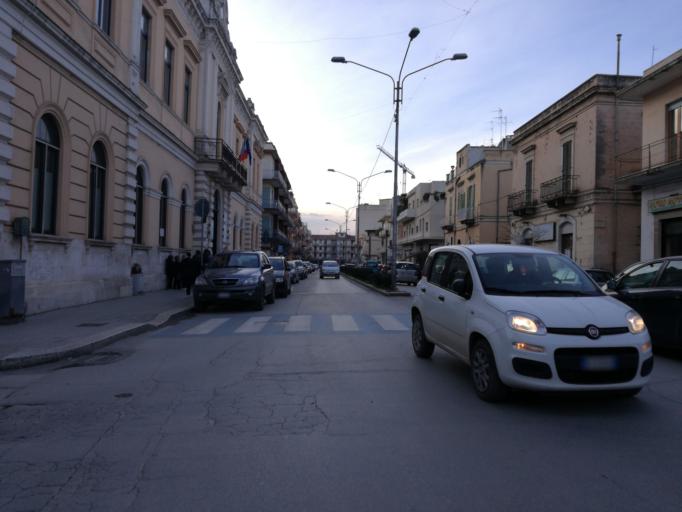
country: IT
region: Apulia
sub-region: Provincia di Bari
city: Corato
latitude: 41.1489
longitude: 16.4117
